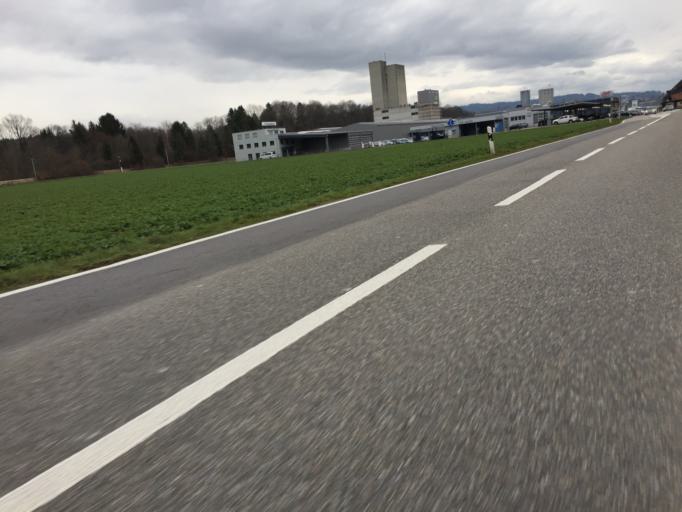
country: CH
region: Bern
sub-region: Emmental District
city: Kirchberg
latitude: 47.0749
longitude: 7.5867
